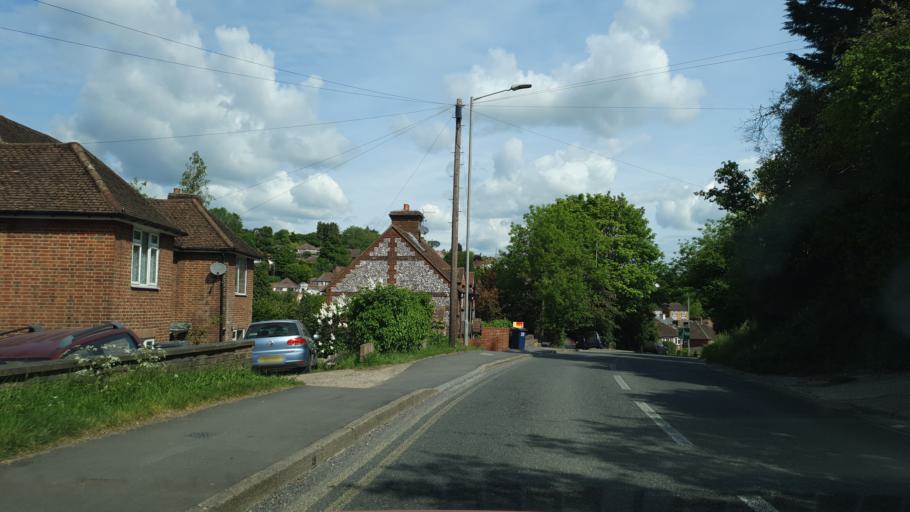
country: GB
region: England
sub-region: Buckinghamshire
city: High Wycombe
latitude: 51.6302
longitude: -0.7854
